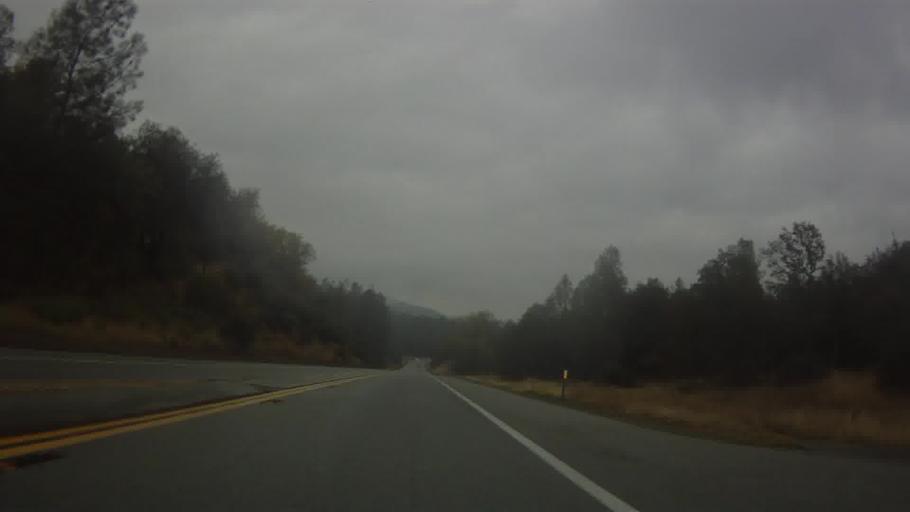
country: US
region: California
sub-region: Shasta County
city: Shasta
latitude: 40.5850
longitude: -122.4486
